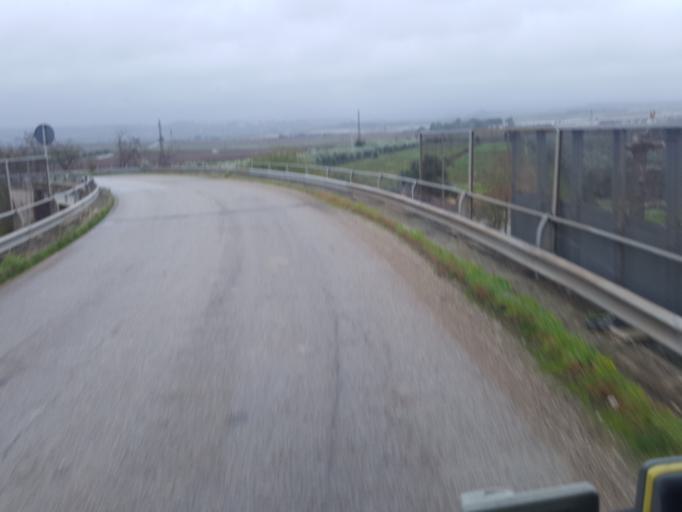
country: IT
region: Apulia
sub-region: Provincia di Taranto
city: Monteiasi
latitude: 40.5243
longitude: 17.3648
